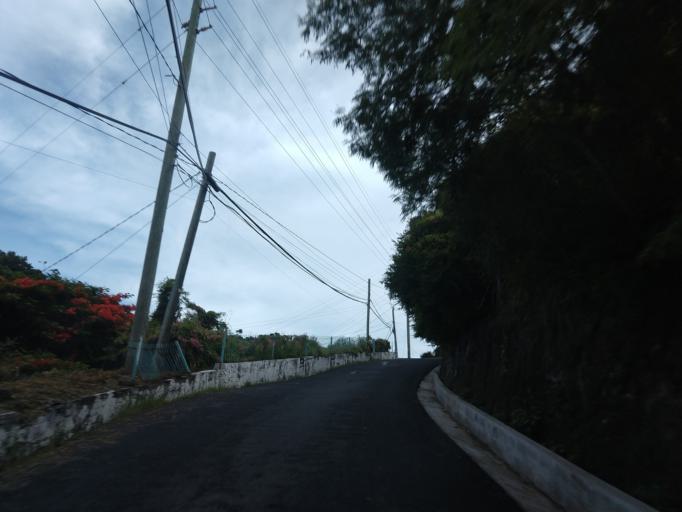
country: GD
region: Saint George
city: Saint George's
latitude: 12.0559
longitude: -61.7536
